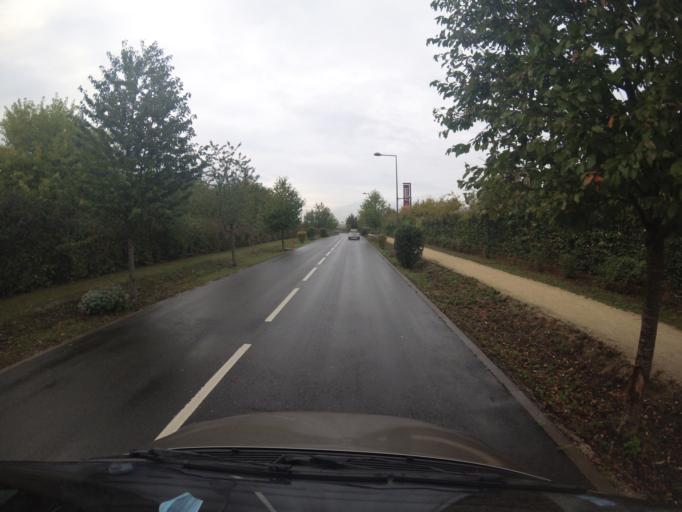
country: FR
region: Ile-de-France
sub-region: Departement de Seine-et-Marne
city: Chanteloup-en-Brie
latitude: 48.8543
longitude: 2.7539
